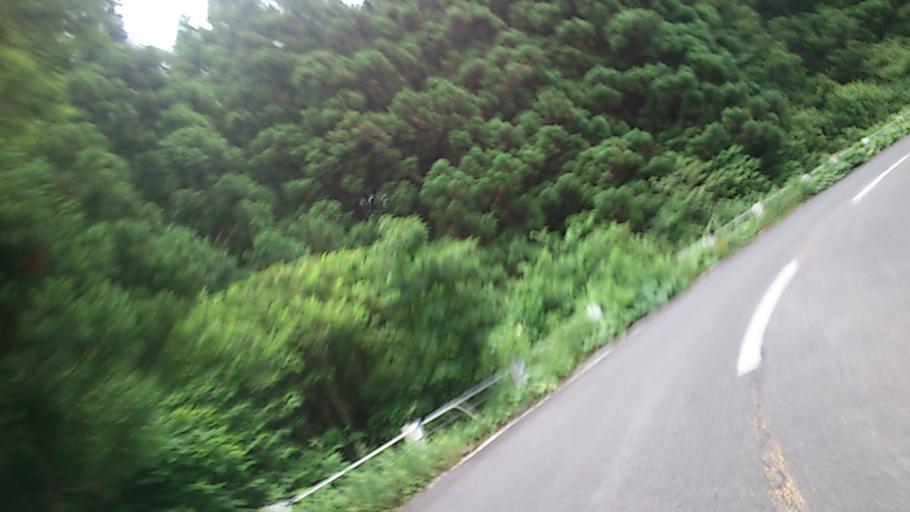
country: JP
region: Yamagata
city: Yuza
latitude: 39.1486
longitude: 139.9646
